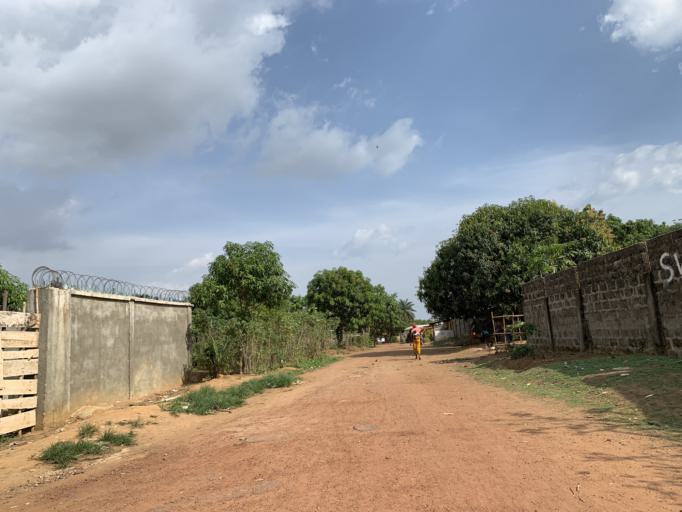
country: SL
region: Western Area
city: Waterloo
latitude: 8.3423
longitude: -13.0464
